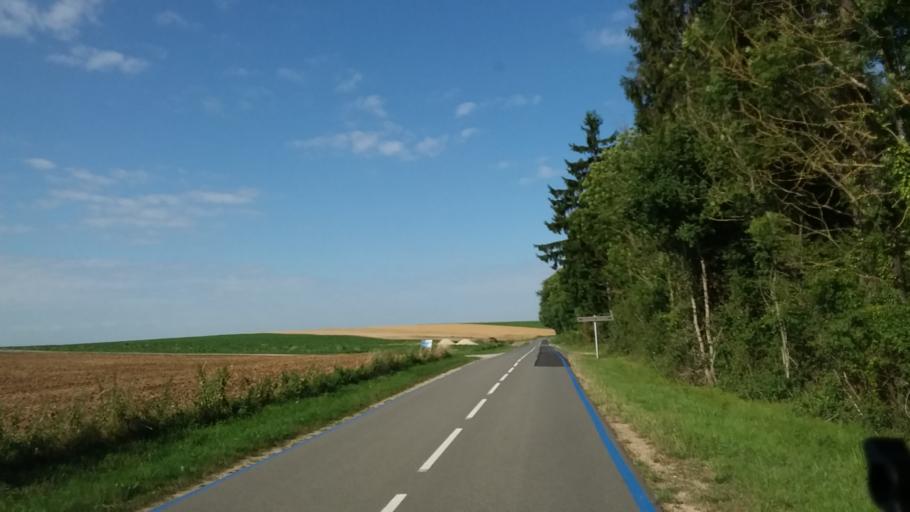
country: FR
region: Picardie
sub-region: Departement de l'Aisne
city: Saint-Erme-Outre-et-Ramecourt
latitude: 49.4409
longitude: 3.7652
